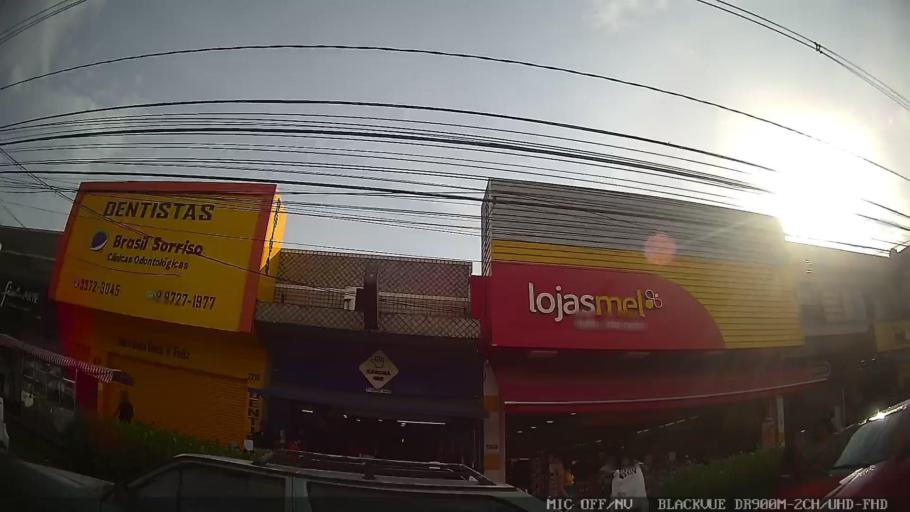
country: BR
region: Sao Paulo
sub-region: Cubatao
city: Cubatao
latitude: -23.8854
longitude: -46.4207
